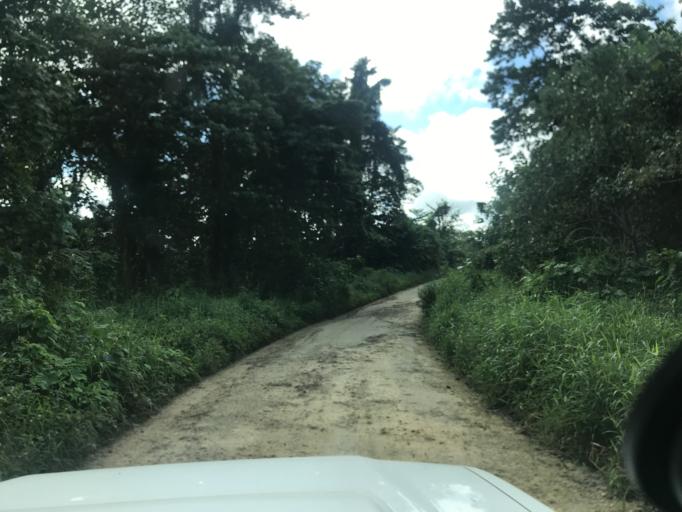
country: VU
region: Sanma
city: Luganville
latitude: -15.4739
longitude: 167.0716
